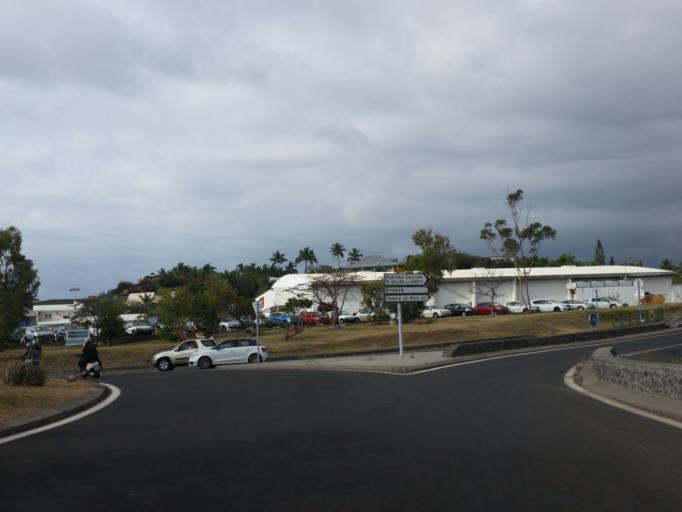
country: RE
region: Reunion
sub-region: Reunion
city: Saint-Paul
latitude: -21.0383
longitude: 55.2193
